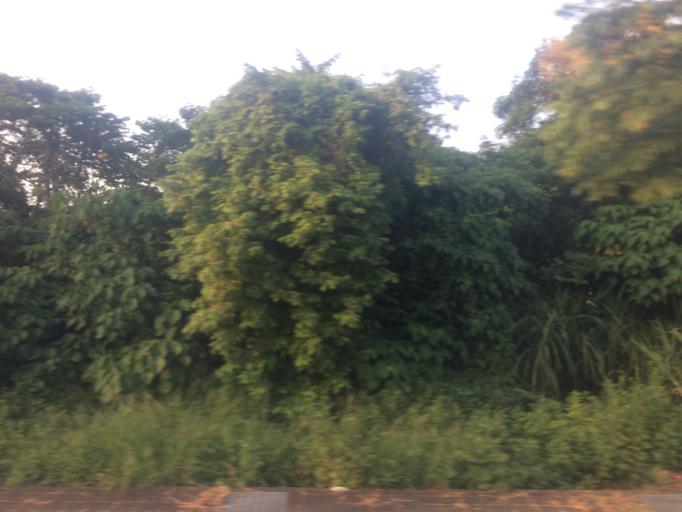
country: TW
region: Taiwan
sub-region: Chiayi
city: Jiayi Shi
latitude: 23.5501
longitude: 120.4269
